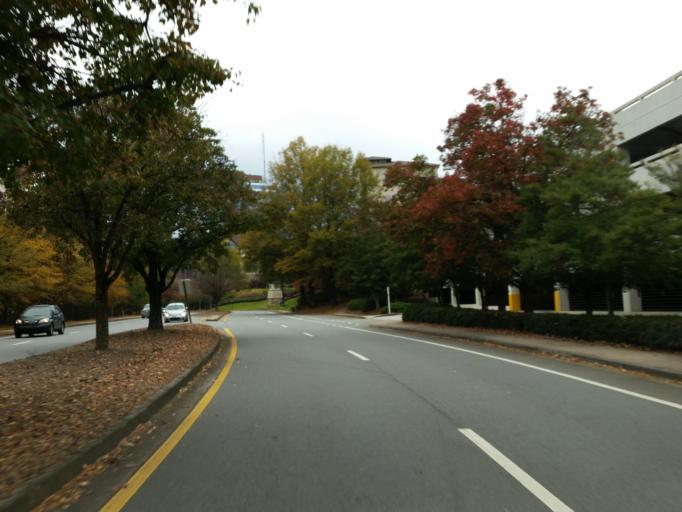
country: US
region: Georgia
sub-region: DeKalb County
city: Dunwoody
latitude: 33.9318
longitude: -84.3408
